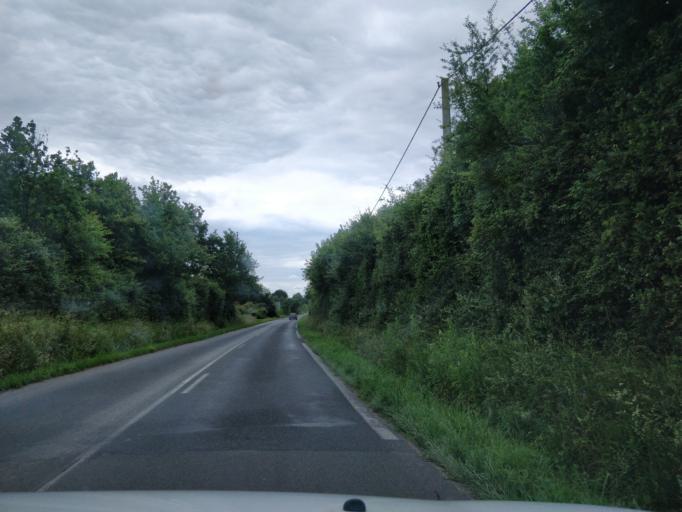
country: FR
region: Pays de la Loire
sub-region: Departement de Maine-et-Loire
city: Feneu
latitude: 47.5654
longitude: -0.5863
